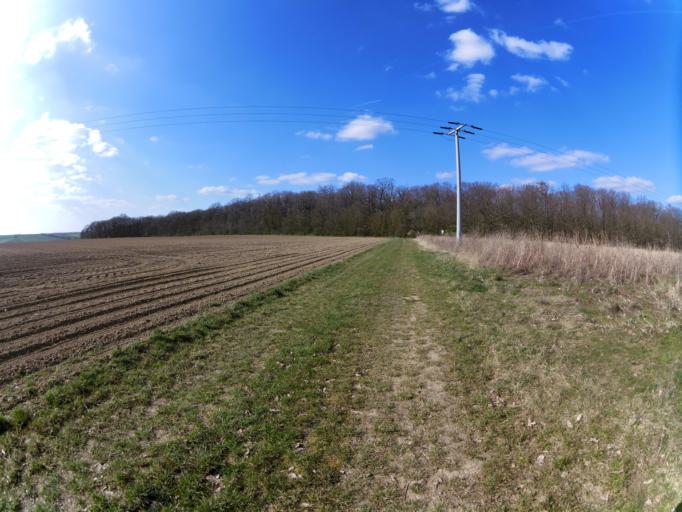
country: DE
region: Bavaria
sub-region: Regierungsbezirk Unterfranken
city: Nordheim
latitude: 49.8452
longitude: 10.1598
